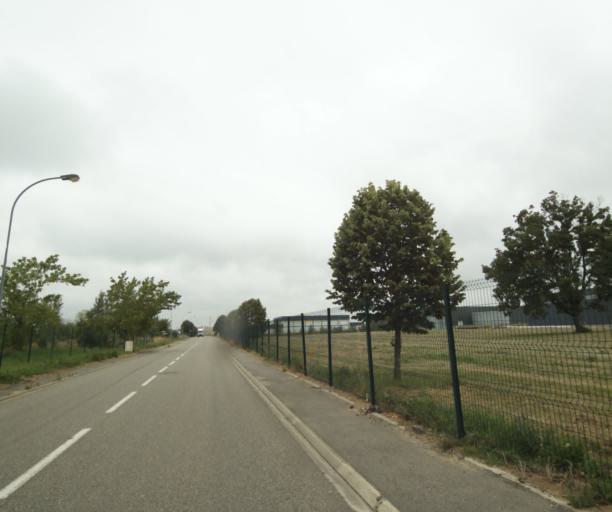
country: FR
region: Midi-Pyrenees
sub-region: Departement du Tarn-et-Garonne
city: Bressols
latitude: 43.9760
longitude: 1.3230
